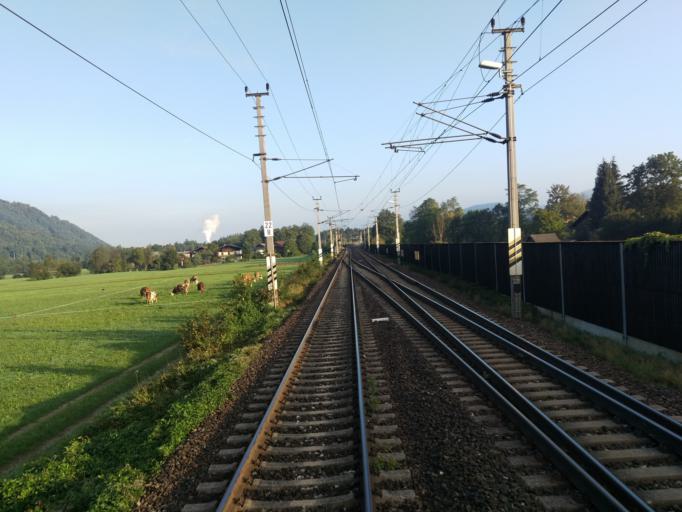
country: AT
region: Salzburg
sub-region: Politischer Bezirk Hallein
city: Kuchl
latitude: 47.6481
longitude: 13.1297
